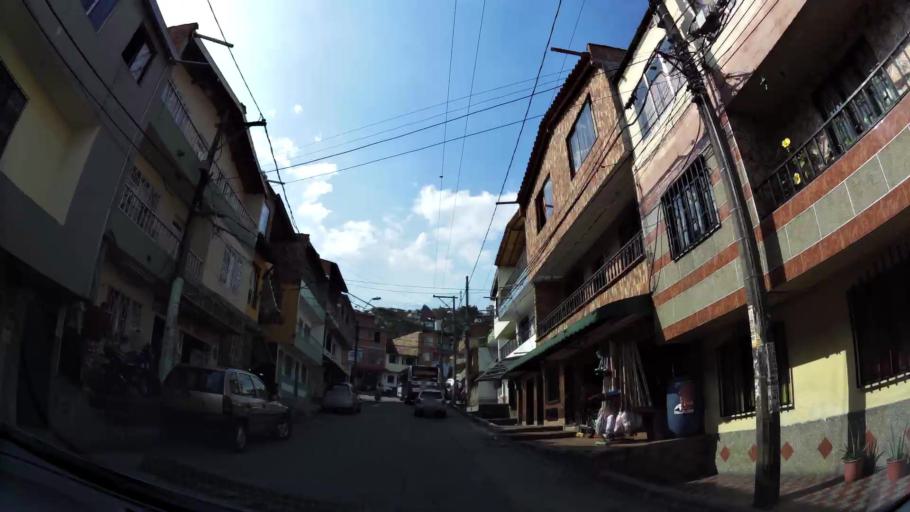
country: CO
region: Antioquia
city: Medellin
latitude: 6.2848
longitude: -75.5908
